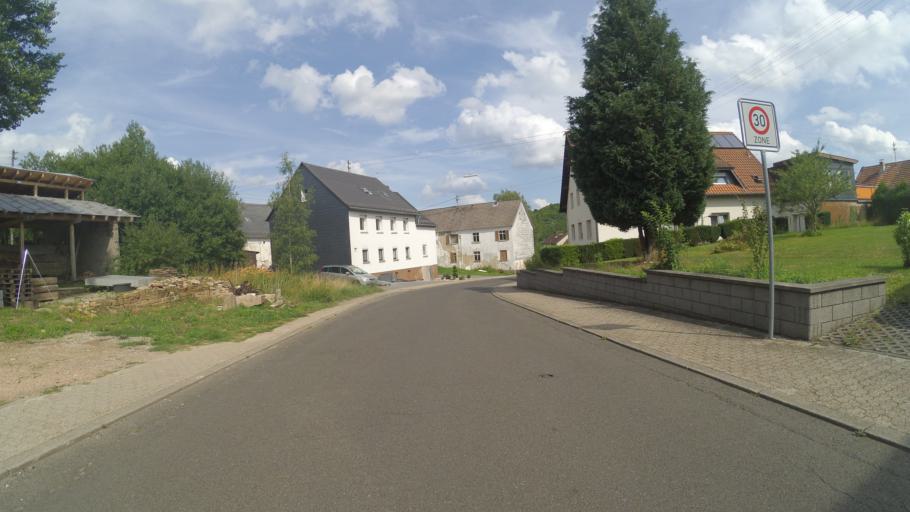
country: DE
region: Rheinland-Pfalz
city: Achtelsbach
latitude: 49.5945
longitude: 7.0654
